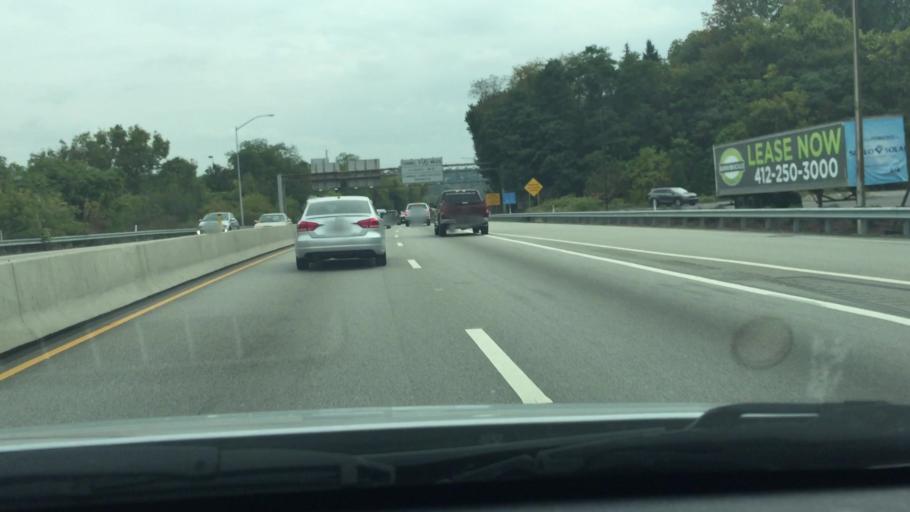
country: US
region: Pennsylvania
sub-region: Allegheny County
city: Green Tree
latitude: 40.4211
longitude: -80.0442
